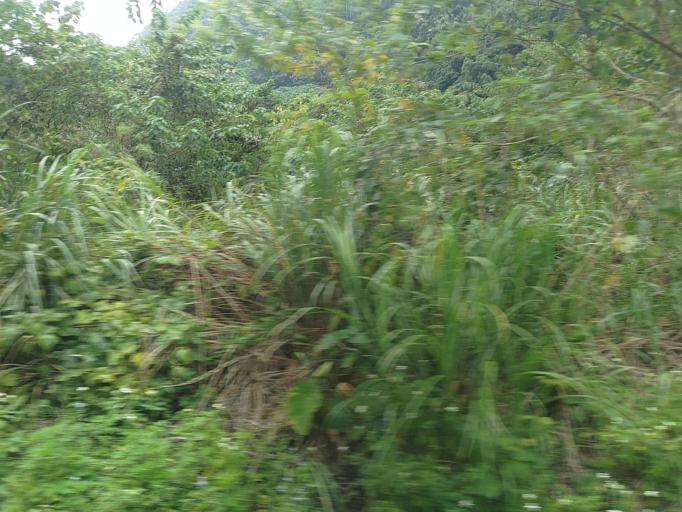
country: TW
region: Taiwan
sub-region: Hsinchu
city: Hsinchu
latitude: 24.6141
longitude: 121.0925
